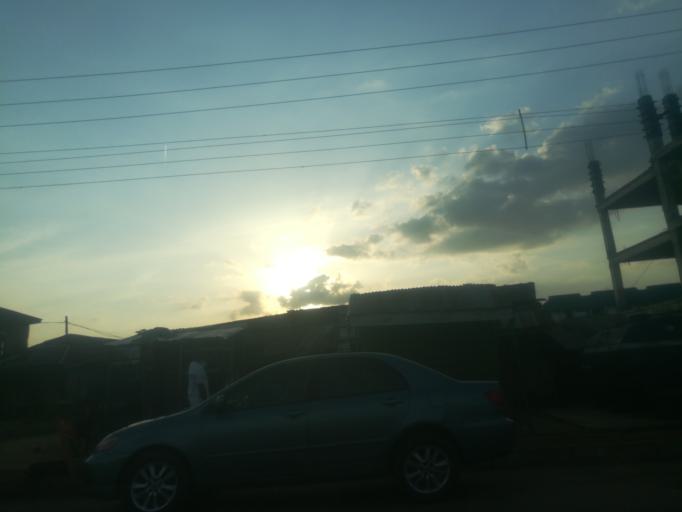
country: NG
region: Ogun
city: Abeokuta
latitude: 7.1398
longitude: 3.3387
